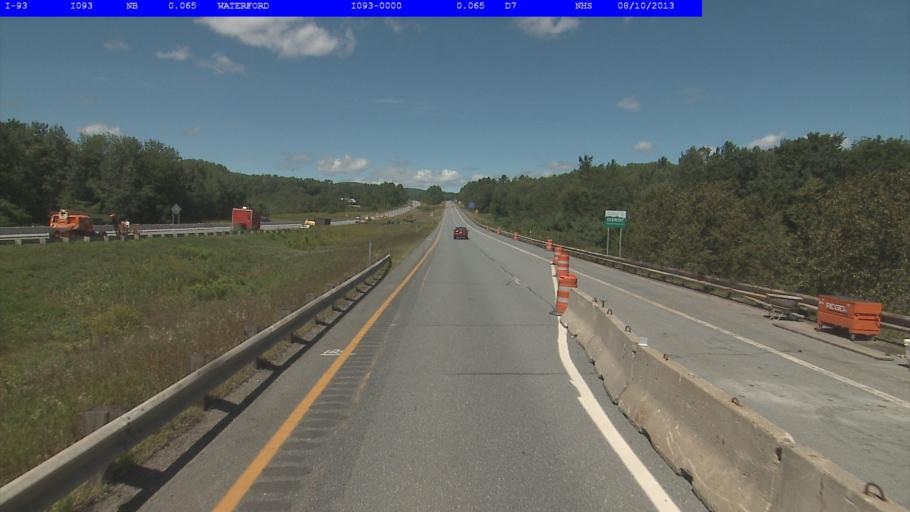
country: US
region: New Hampshire
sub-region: Grafton County
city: Littleton
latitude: 44.3440
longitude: -71.8912
